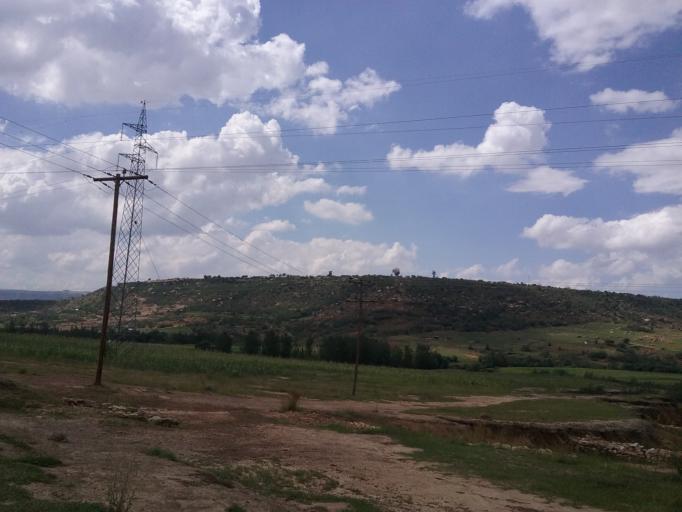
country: LS
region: Maseru
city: Maseru
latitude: -29.4179
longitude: 27.5718
